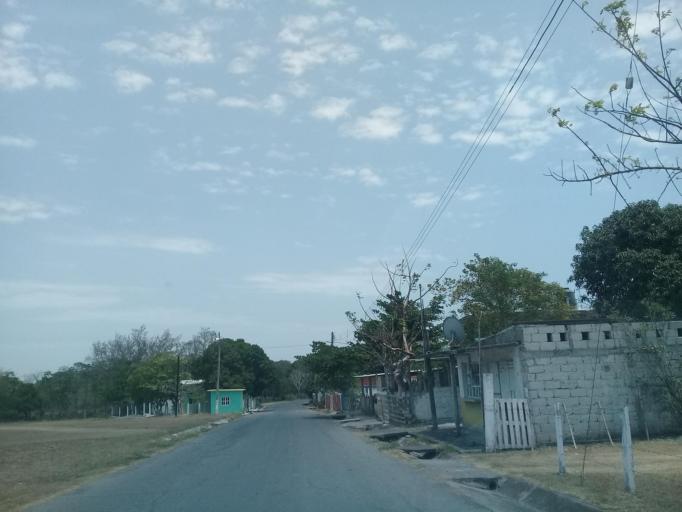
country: MX
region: Veracruz
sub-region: Veracruz
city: Delfino Victoria (Santa Fe)
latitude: 19.1711
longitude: -96.2976
